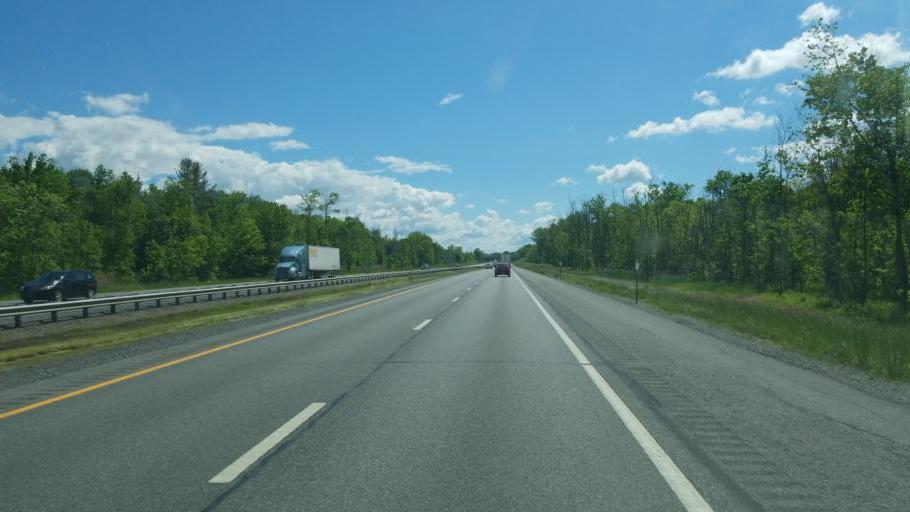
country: US
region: New York
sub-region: Madison County
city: Wampsville
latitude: 43.1054
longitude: -75.6915
